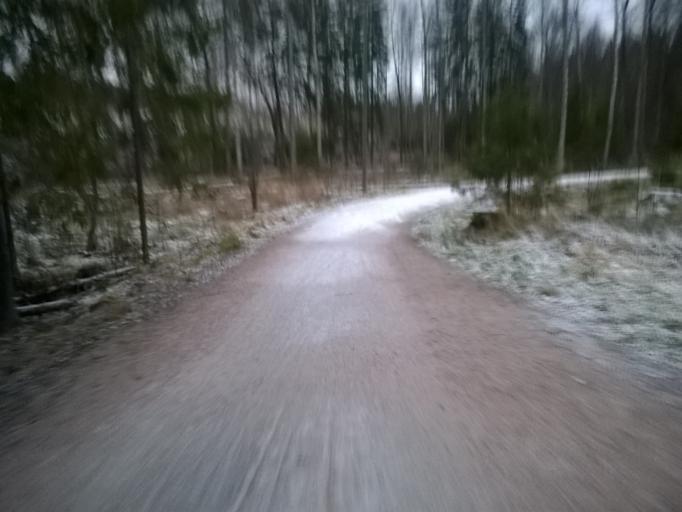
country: FI
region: Uusimaa
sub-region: Helsinki
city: Helsinki
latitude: 60.2541
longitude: 24.9057
